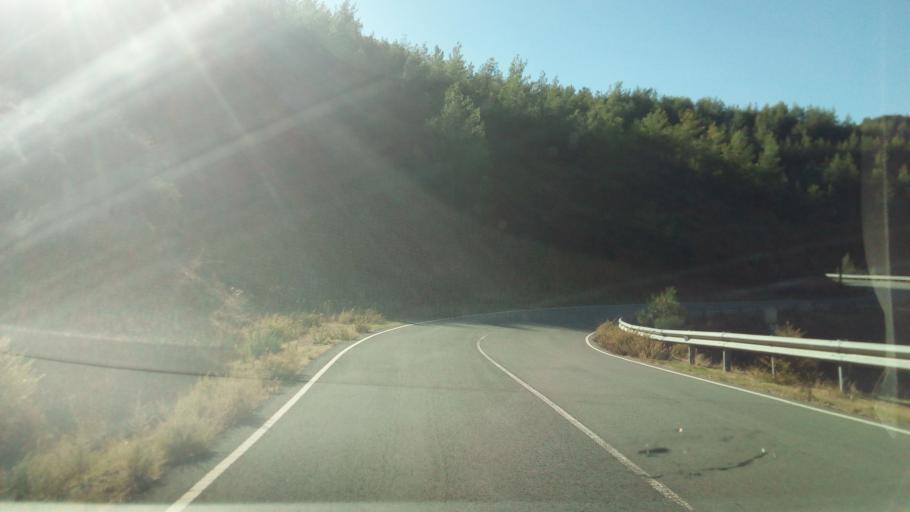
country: CY
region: Lefkosia
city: Kato Pyrgos
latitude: 35.1168
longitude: 32.7310
